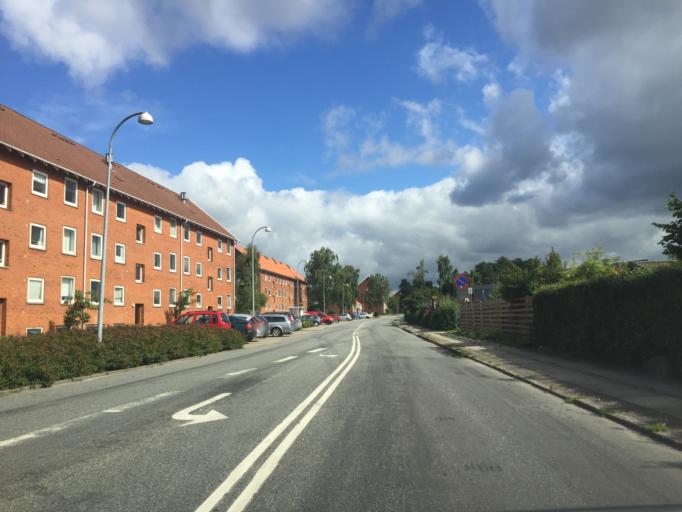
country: DK
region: Capital Region
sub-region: Brondby Kommune
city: Brondbyvester
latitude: 55.6532
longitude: 12.4117
